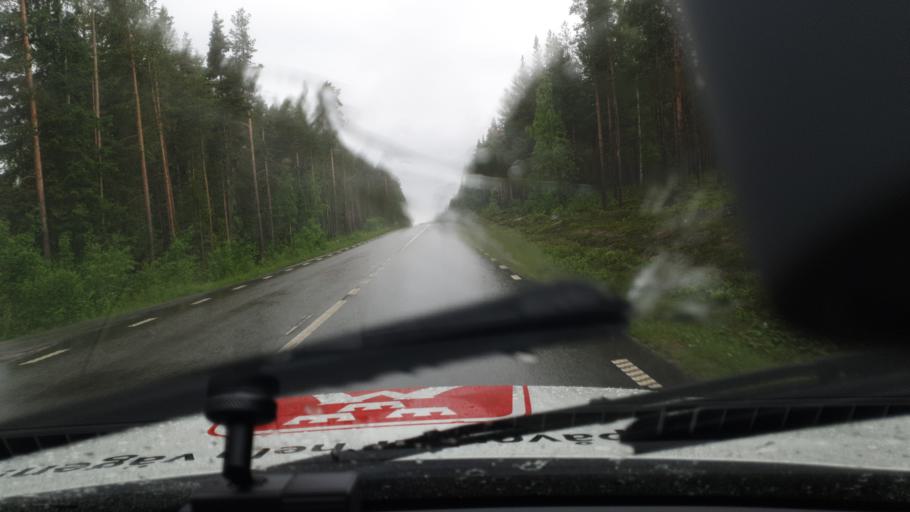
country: SE
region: Vaesterbotten
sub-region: Lycksele Kommun
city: Lycksele
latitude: 64.5551
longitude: 18.7316
